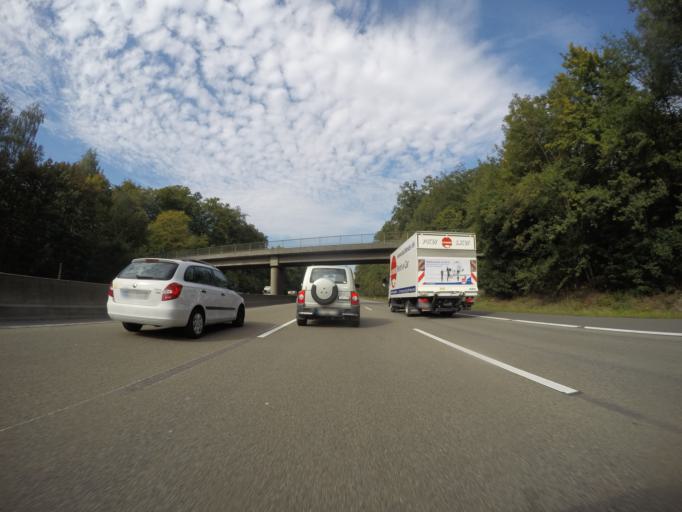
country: DE
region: Hesse
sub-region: Regierungsbezirk Darmstadt
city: Seligenstadt
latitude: 50.0183
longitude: 8.9572
